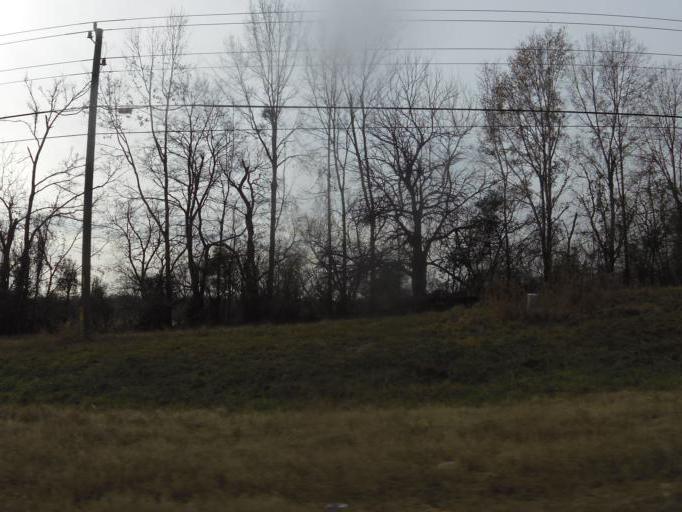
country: US
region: Alabama
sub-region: Montgomery County
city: Pike Road
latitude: 32.2989
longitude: -86.2006
